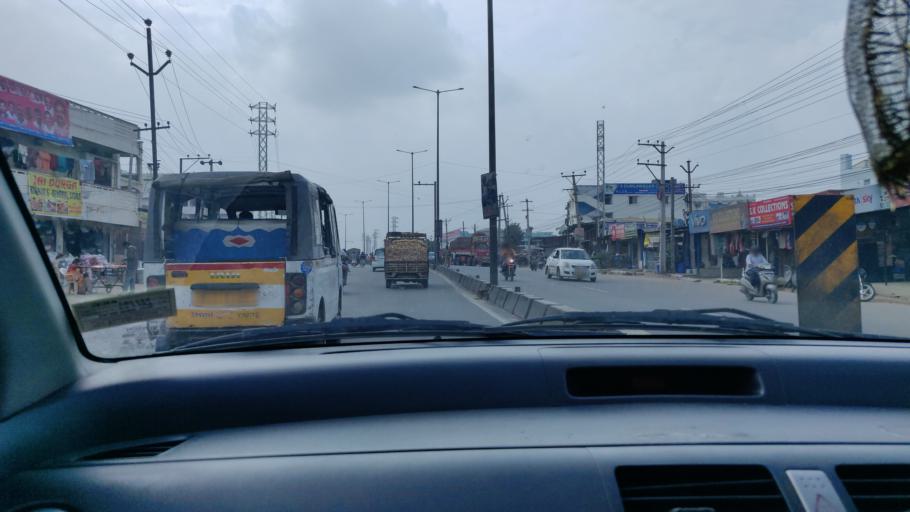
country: IN
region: Telangana
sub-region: Rangareddi
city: Balapur
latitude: 17.3160
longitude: 78.4489
